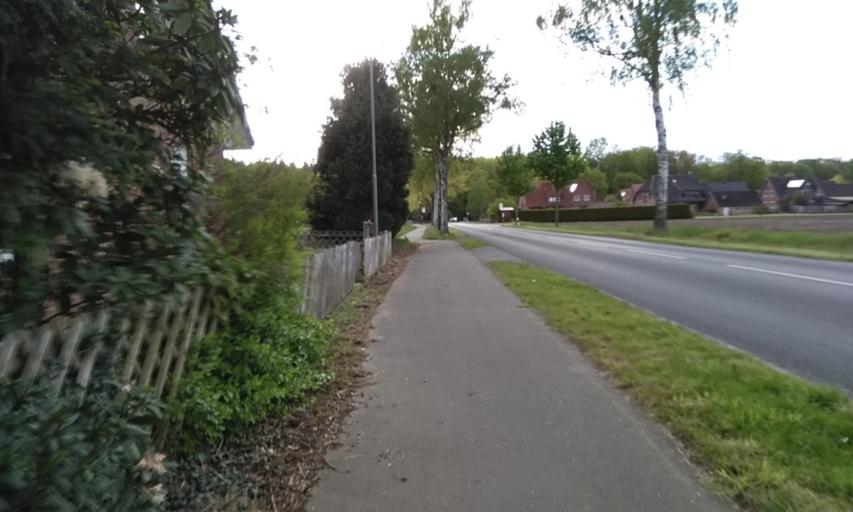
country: DE
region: Lower Saxony
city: Wohnste
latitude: 53.3883
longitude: 9.5427
